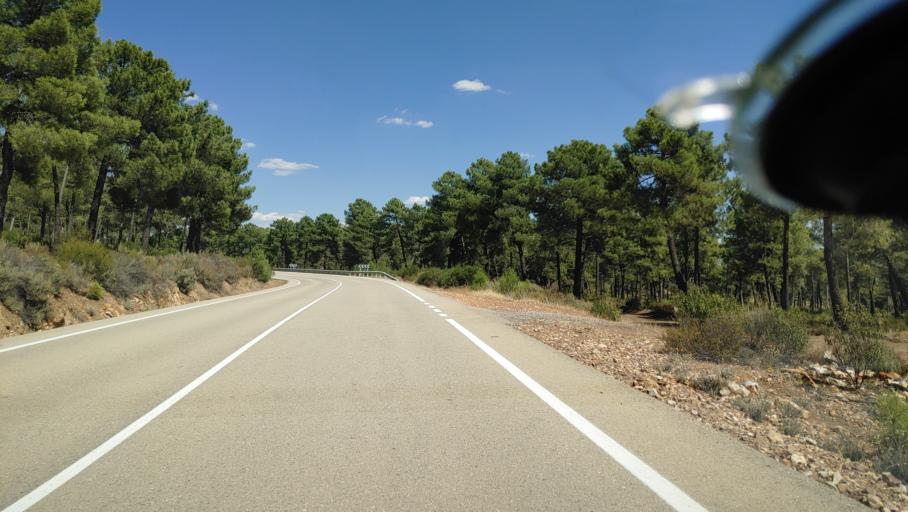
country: ES
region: Castille-La Mancha
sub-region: Provincia de Ciudad Real
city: Saceruela
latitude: 38.9986
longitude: -4.5167
